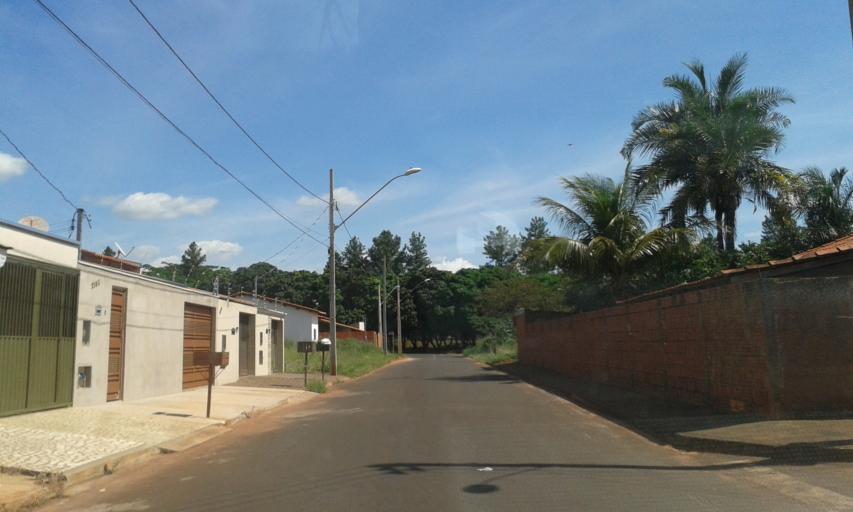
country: BR
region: Minas Gerais
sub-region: Santa Vitoria
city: Santa Vitoria
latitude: -18.8554
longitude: -50.1287
